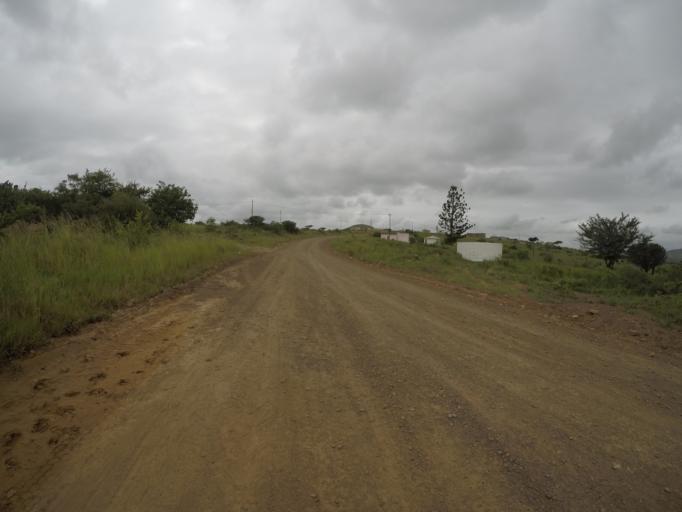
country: ZA
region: KwaZulu-Natal
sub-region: uThungulu District Municipality
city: Empangeni
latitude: -28.6032
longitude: 31.8391
